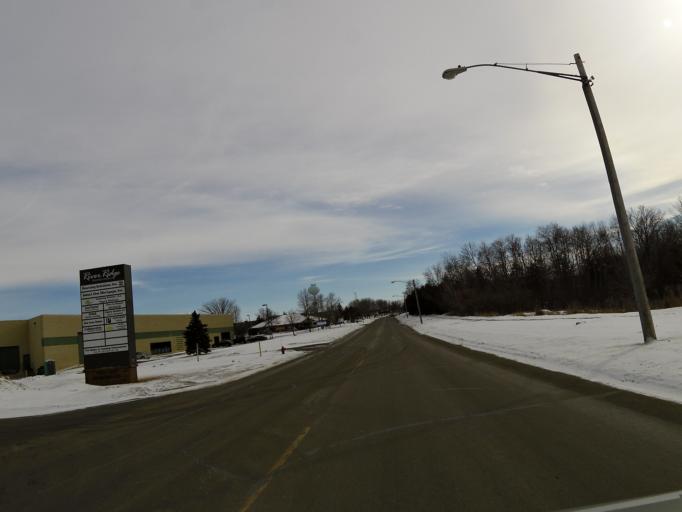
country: US
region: Wisconsin
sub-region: Saint Croix County
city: Hudson
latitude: 44.9589
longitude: -92.7419
